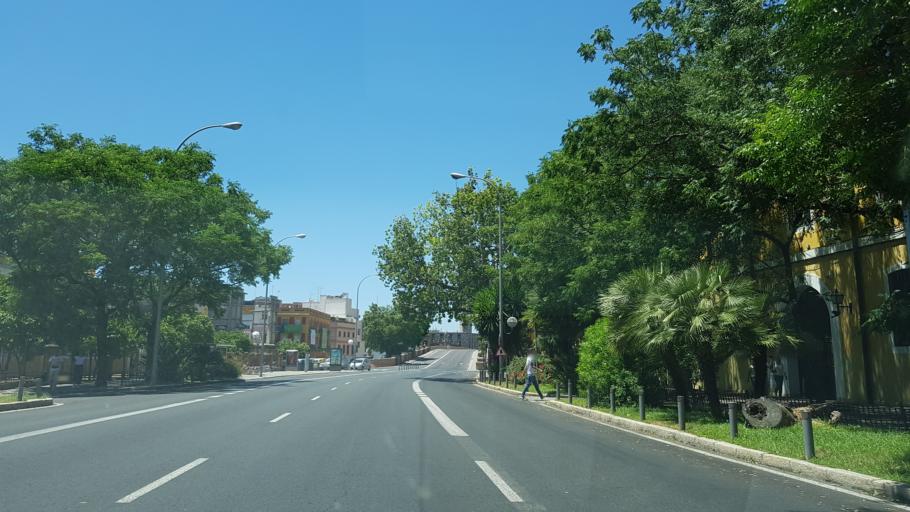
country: ES
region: Andalusia
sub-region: Provincia de Sevilla
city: Sevilla
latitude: 37.3844
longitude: -5.9815
